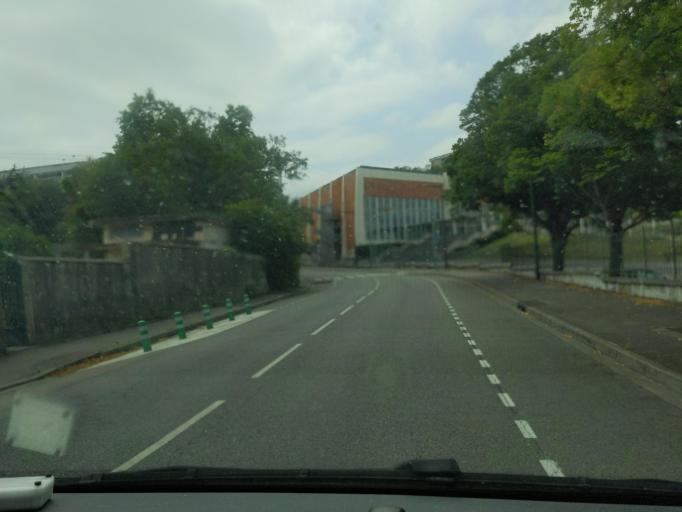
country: FR
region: Midi-Pyrenees
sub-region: Departement de la Haute-Garonne
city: Ramonville-Saint-Agne
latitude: 43.5617
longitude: 1.4586
